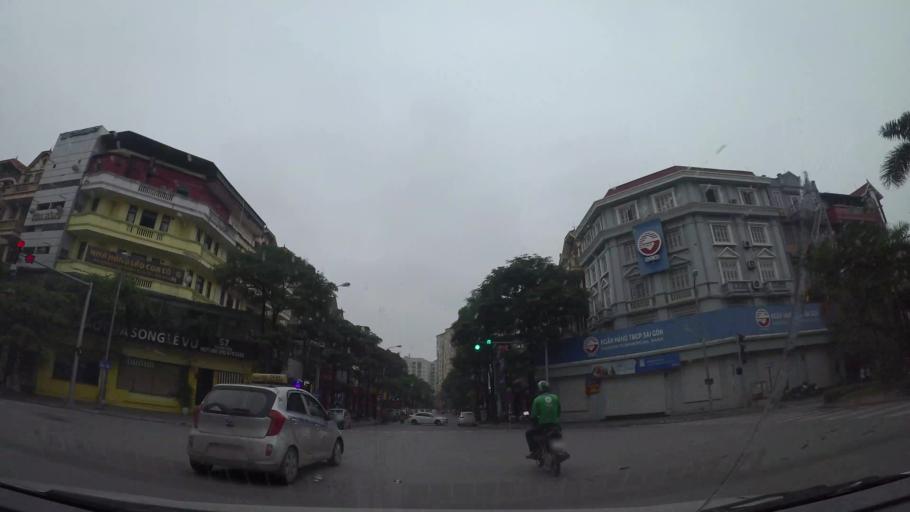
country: VN
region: Ha Noi
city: Cau Giay
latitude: 21.0156
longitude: 105.8008
